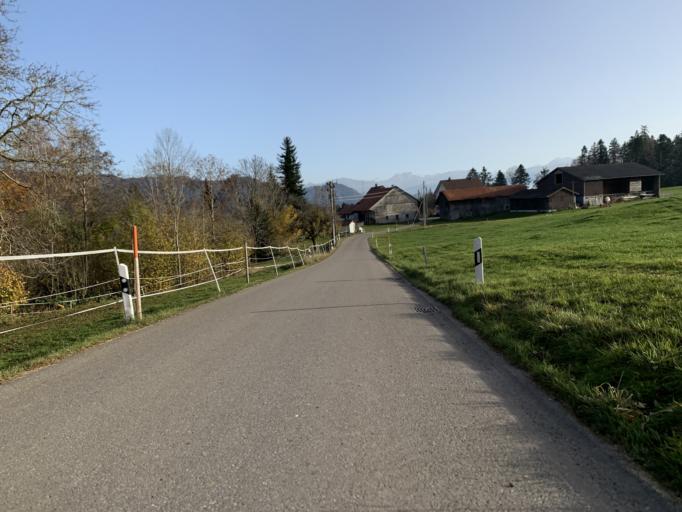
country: CH
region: Zurich
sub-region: Bezirk Hinwil
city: Wald
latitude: 47.3111
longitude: 8.9004
